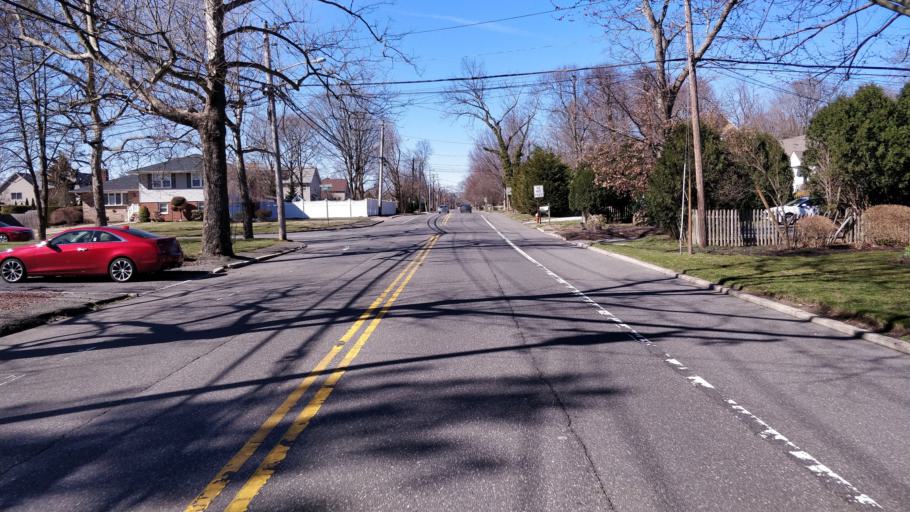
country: US
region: New York
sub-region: Suffolk County
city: Commack
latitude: 40.8507
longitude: -73.3031
